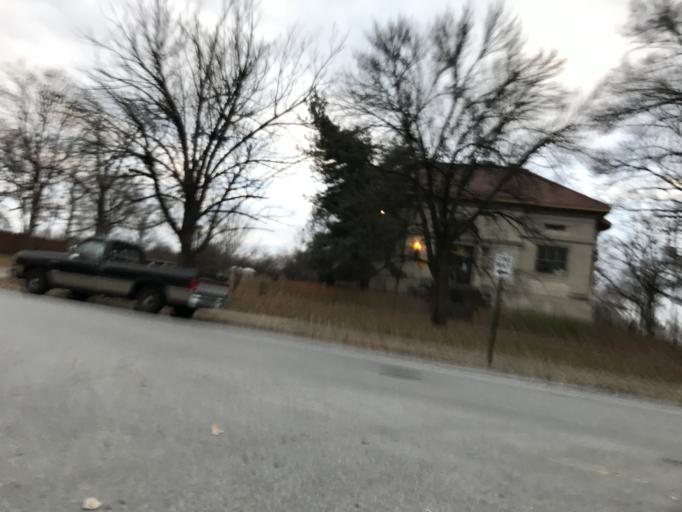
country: US
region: Kentucky
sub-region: Jefferson County
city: Louisville
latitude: 38.2341
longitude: -85.7455
